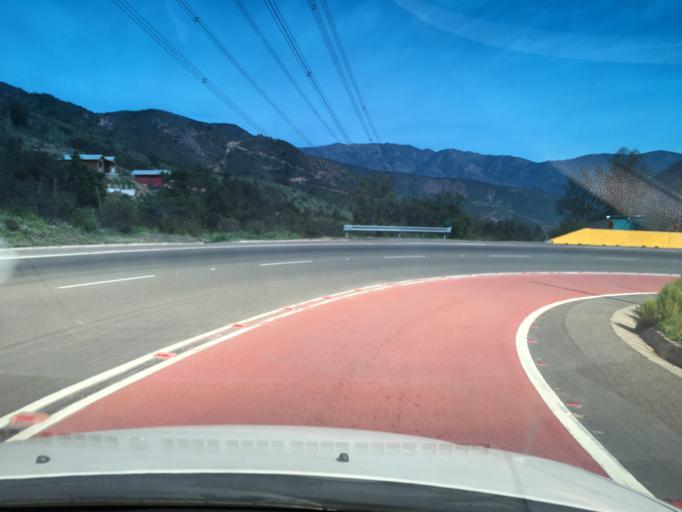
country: CL
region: Valparaiso
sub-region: Provincia de Marga Marga
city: Limache
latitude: -33.0588
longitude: -71.0451
